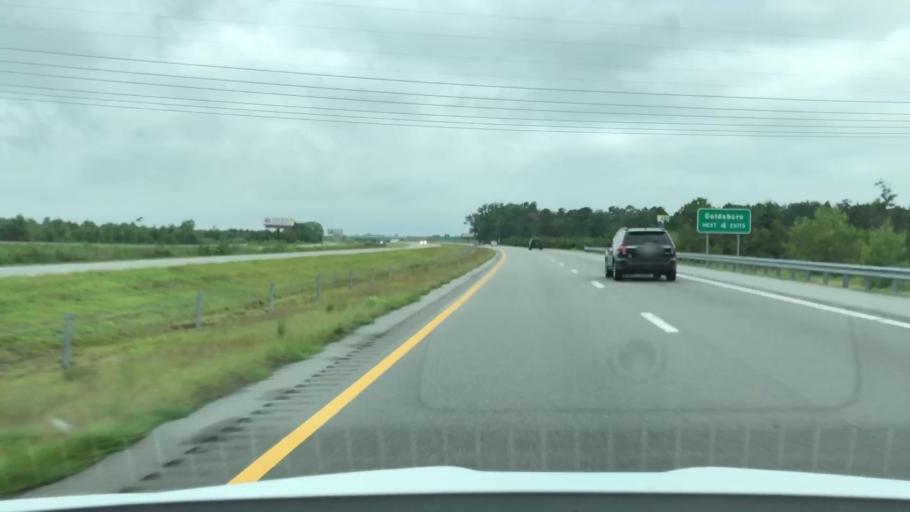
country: US
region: North Carolina
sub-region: Wayne County
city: Elroy
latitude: 35.3990
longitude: -77.8712
